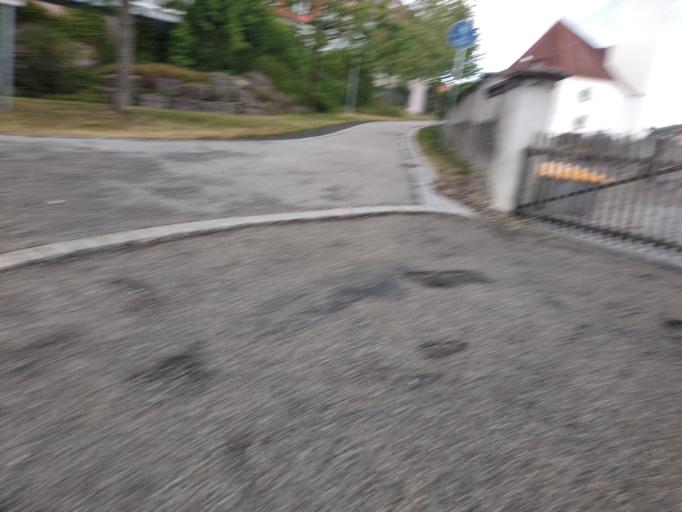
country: DE
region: Bavaria
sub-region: Swabia
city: Dietmannsried
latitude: 47.8074
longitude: 10.2886
